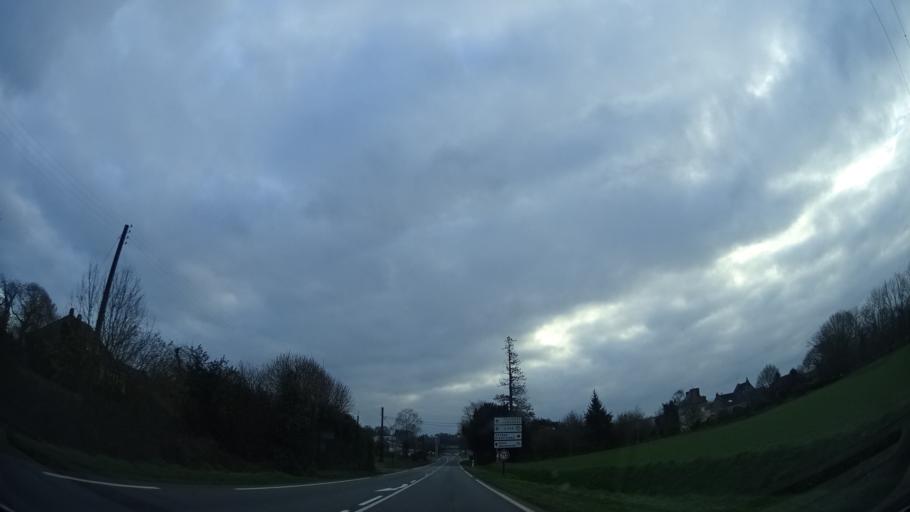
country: FR
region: Brittany
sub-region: Departement d'Ille-et-Vilaine
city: Poce-les-Bois
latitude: 48.1231
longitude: -1.2382
